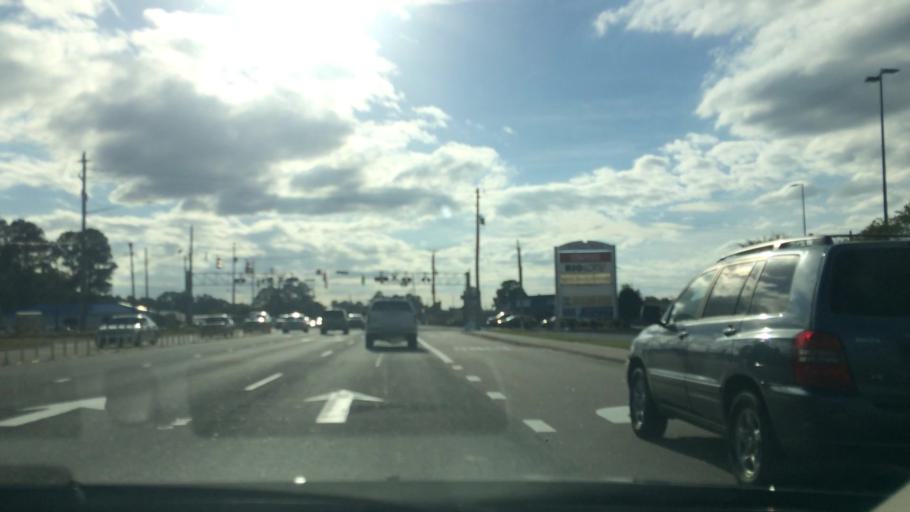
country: US
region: North Carolina
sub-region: Wayne County
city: Elroy
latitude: 35.3803
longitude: -77.9332
